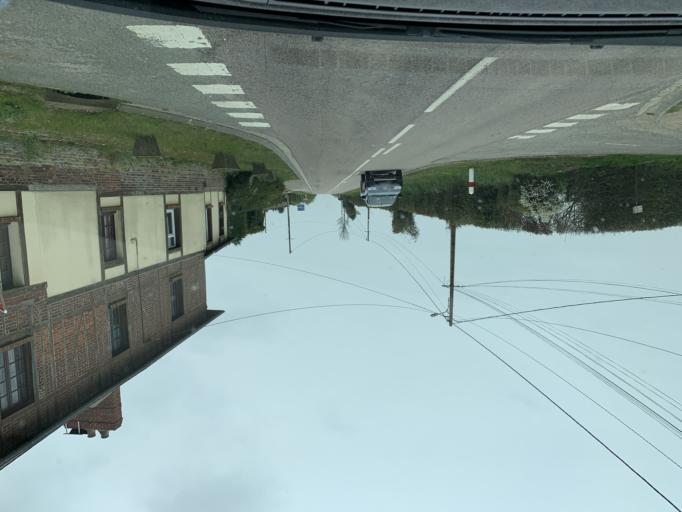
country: FR
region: Haute-Normandie
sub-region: Departement de la Seine-Maritime
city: Foucarmont
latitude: 49.8322
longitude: 1.5205
